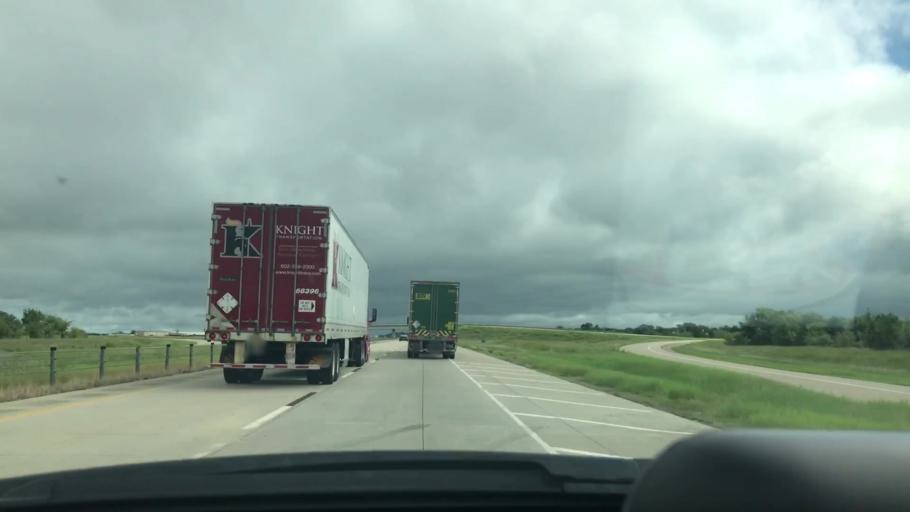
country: US
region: Oklahoma
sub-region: Bryan County
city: Durant
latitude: 34.0928
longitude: -96.3243
